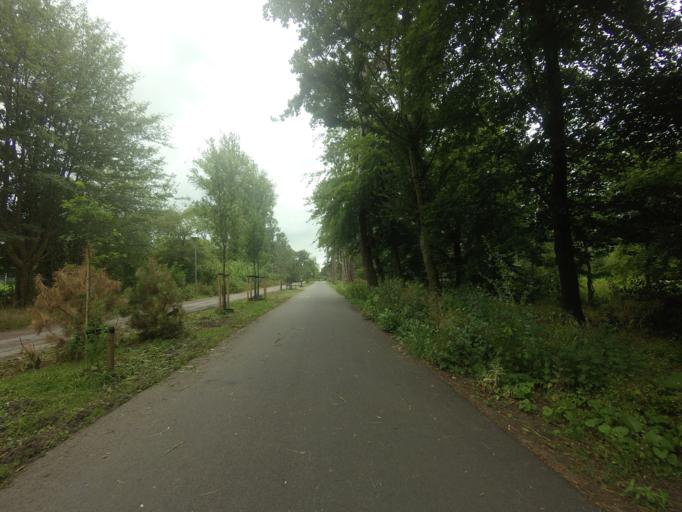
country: NL
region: North Holland
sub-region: Gemeente Bloemendaal
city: Bloemendaal
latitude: 52.4124
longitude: 4.6457
